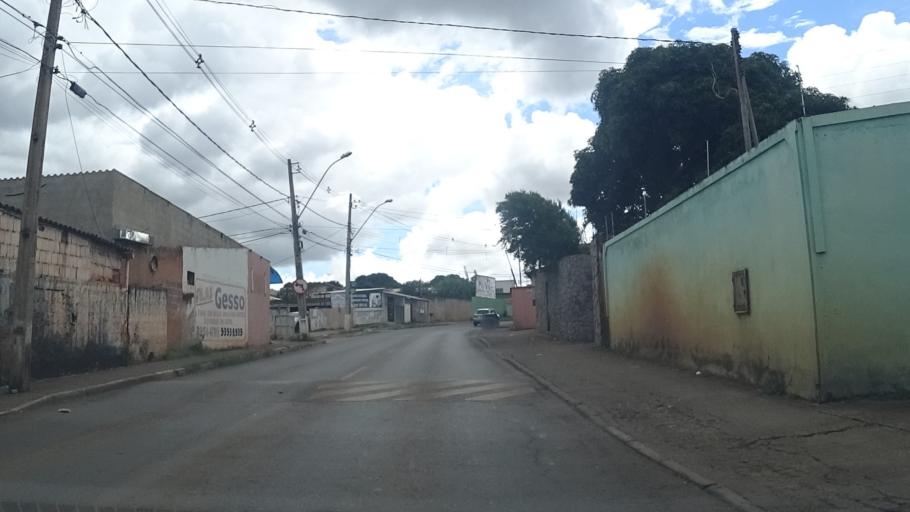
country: BR
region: Federal District
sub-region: Brasilia
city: Brasilia
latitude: -15.8486
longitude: -48.0267
